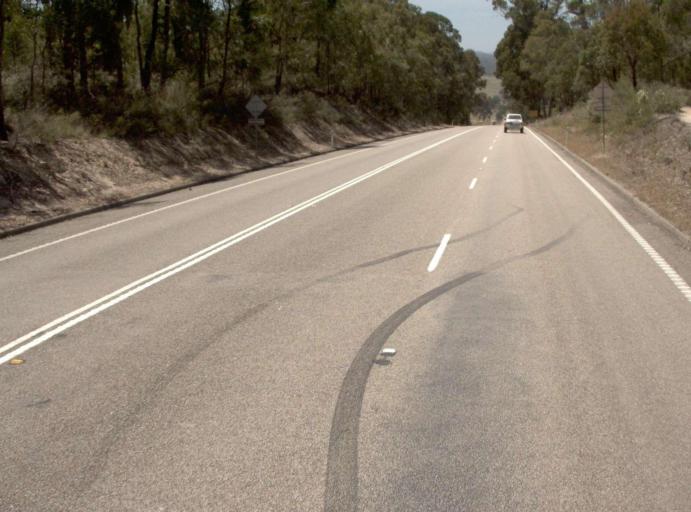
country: AU
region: Victoria
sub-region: East Gippsland
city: Bairnsdale
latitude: -37.7736
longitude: 147.6895
